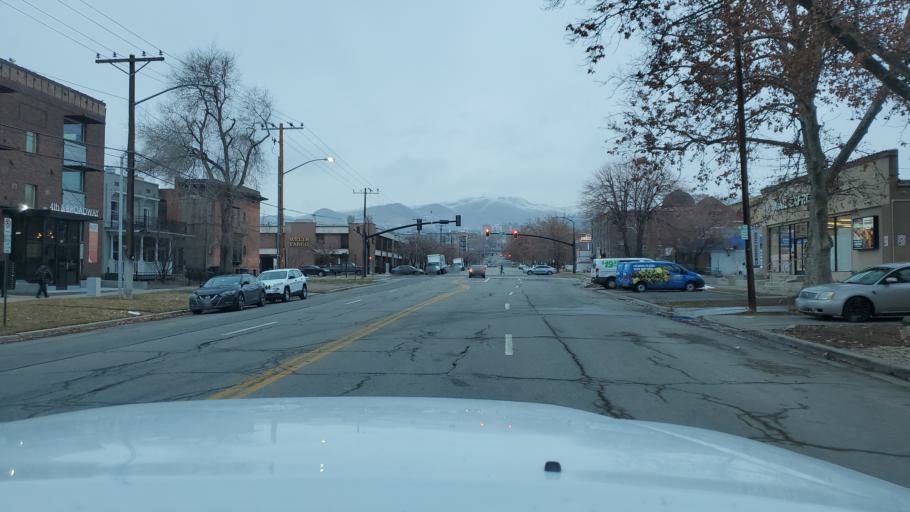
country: US
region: Utah
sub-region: Salt Lake County
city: Salt Lake City
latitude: 40.7619
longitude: -111.8796
